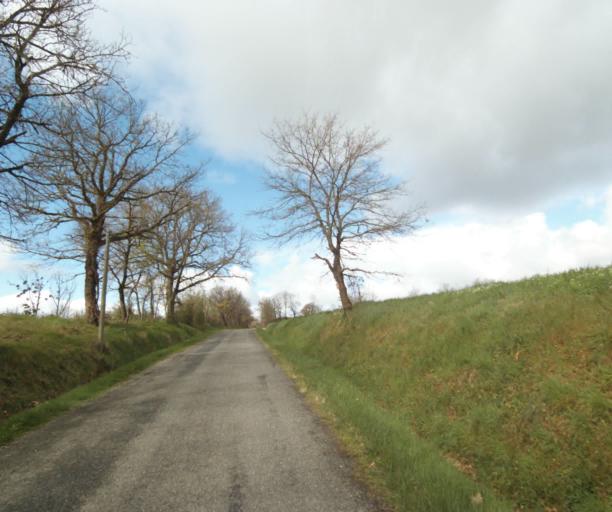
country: FR
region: Midi-Pyrenees
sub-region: Departement de l'Ariege
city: Saverdun
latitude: 43.2327
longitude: 1.5582
